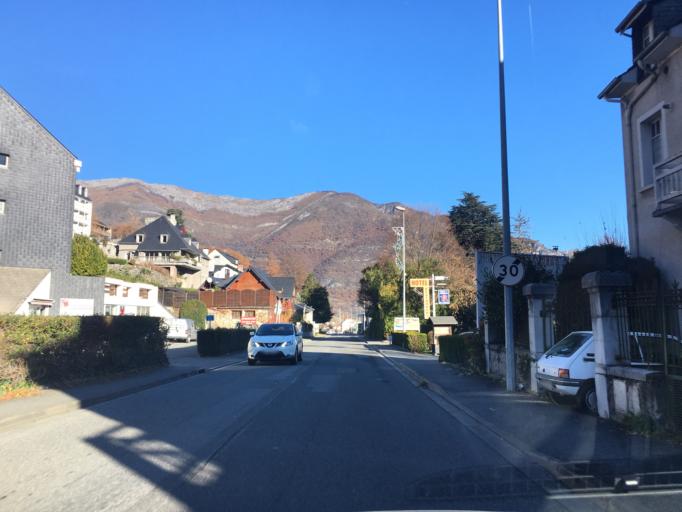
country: FR
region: Midi-Pyrenees
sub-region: Departement des Hautes-Pyrenees
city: Argeles-Gazost
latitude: 43.0073
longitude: -0.0985
